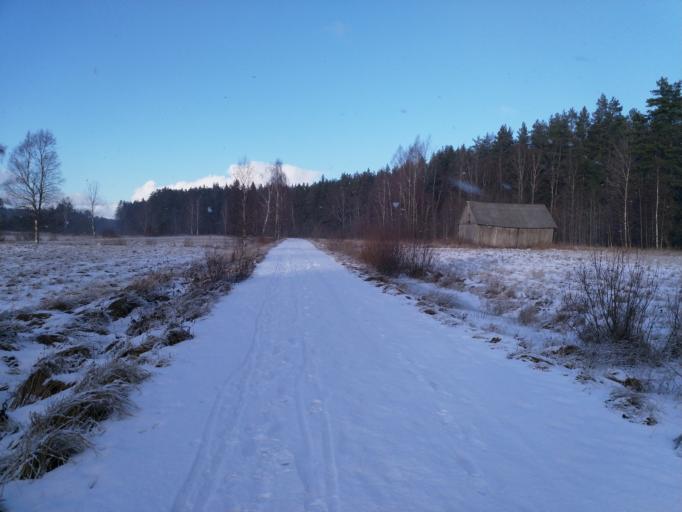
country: LV
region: Skrunda
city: Skrunda
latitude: 56.6734
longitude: 22.0839
